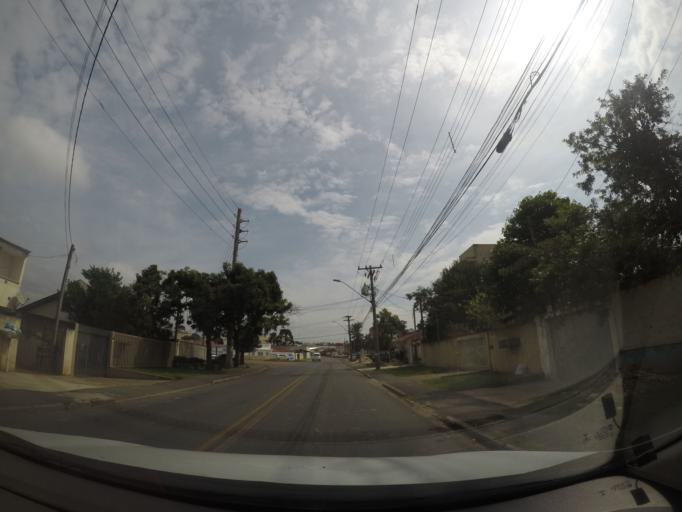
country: BR
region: Parana
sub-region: Sao Jose Dos Pinhais
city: Sao Jose dos Pinhais
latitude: -25.5222
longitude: -49.2813
